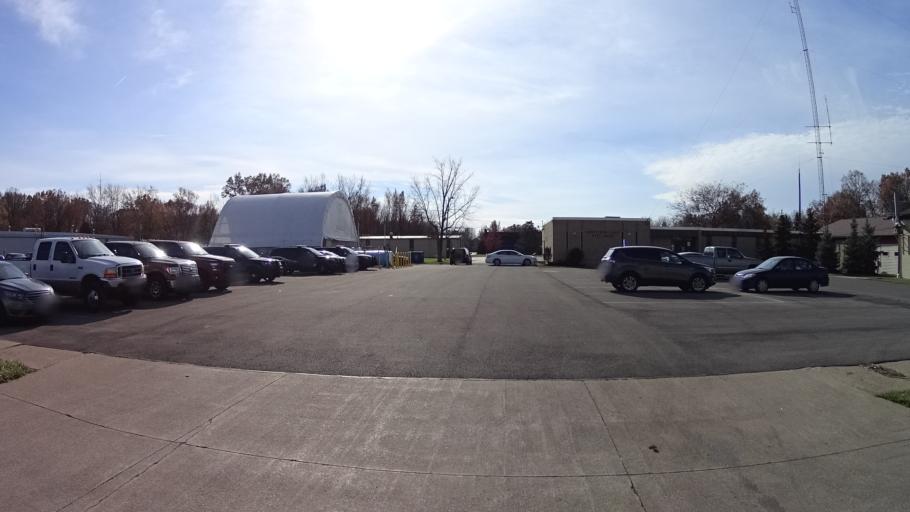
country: US
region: Ohio
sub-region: Lorain County
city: Sheffield Lake
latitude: 41.4902
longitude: -82.0937
